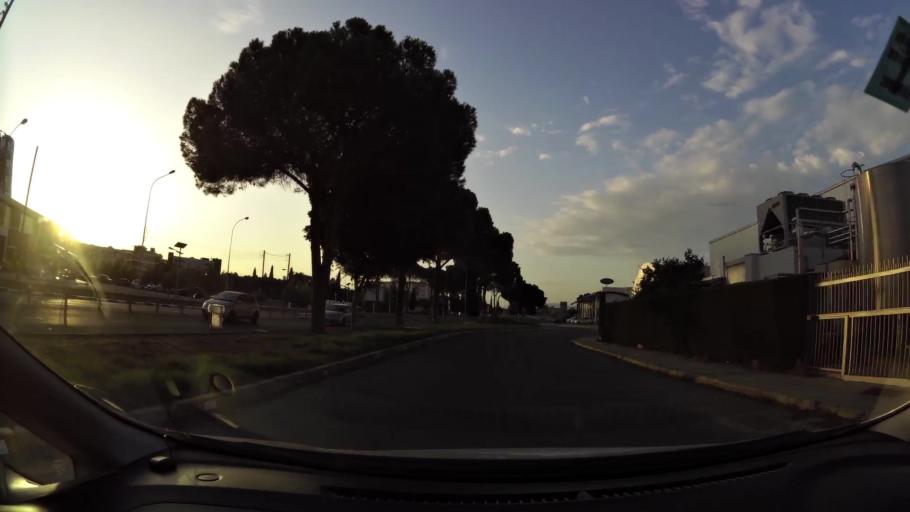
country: CY
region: Lefkosia
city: Nicosia
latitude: 35.1660
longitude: 33.3178
